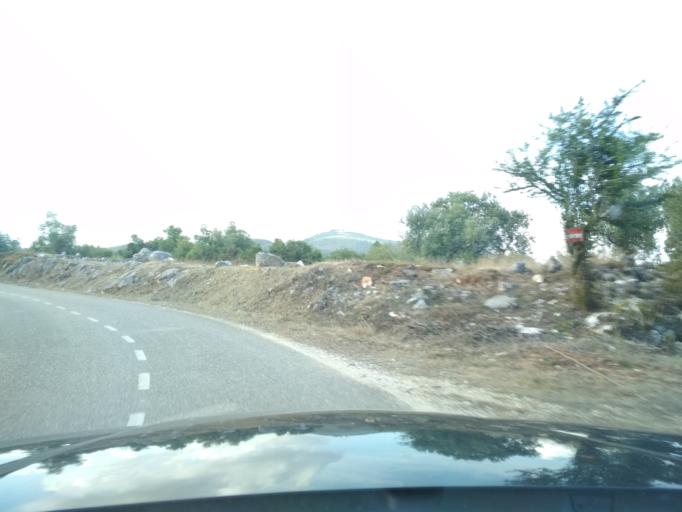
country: PT
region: Coimbra
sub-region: Condeixa-A-Nova
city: Condeixa-a-Nova
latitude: 40.0777
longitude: -8.5064
